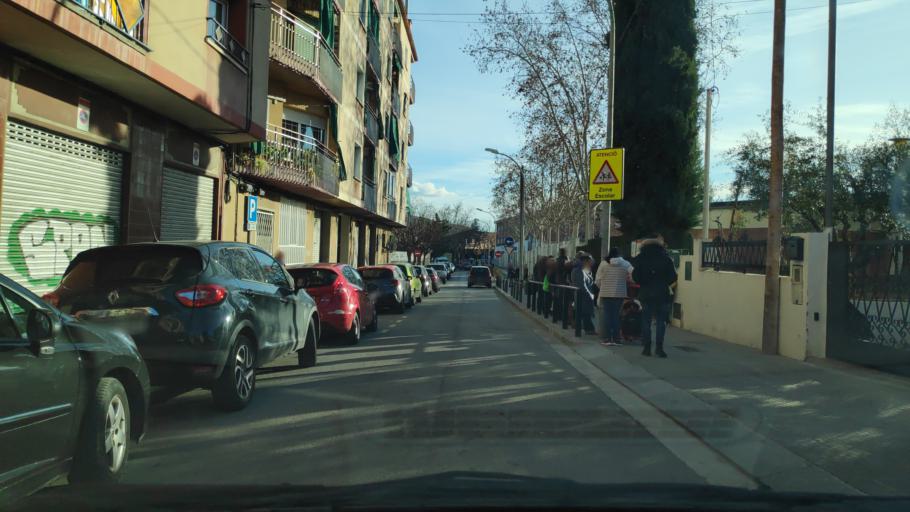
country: ES
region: Catalonia
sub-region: Provincia de Barcelona
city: Mollet del Valles
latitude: 41.5344
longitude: 2.2065
